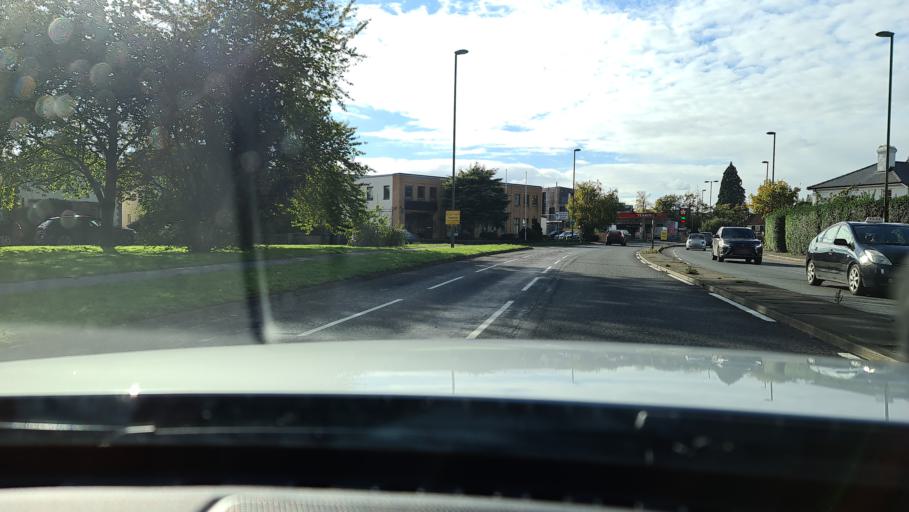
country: GB
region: England
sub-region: Surrey
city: Esher
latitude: 51.3684
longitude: -0.3938
